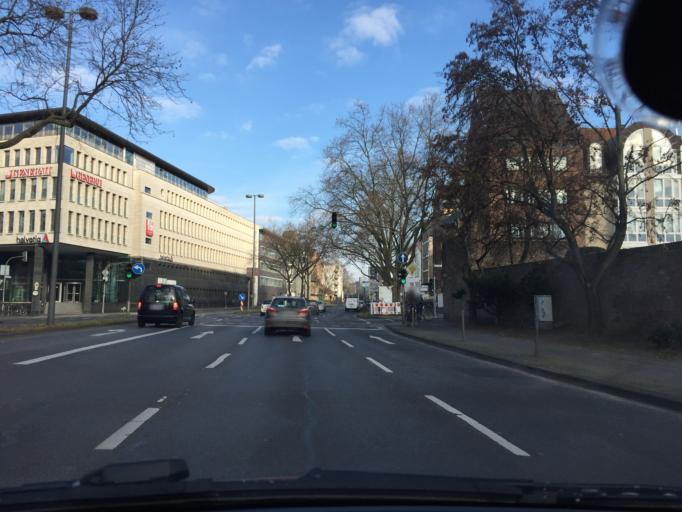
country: DE
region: North Rhine-Westphalia
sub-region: Regierungsbezirk Koln
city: Neustadt/Sued
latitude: 50.9254
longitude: 6.9537
